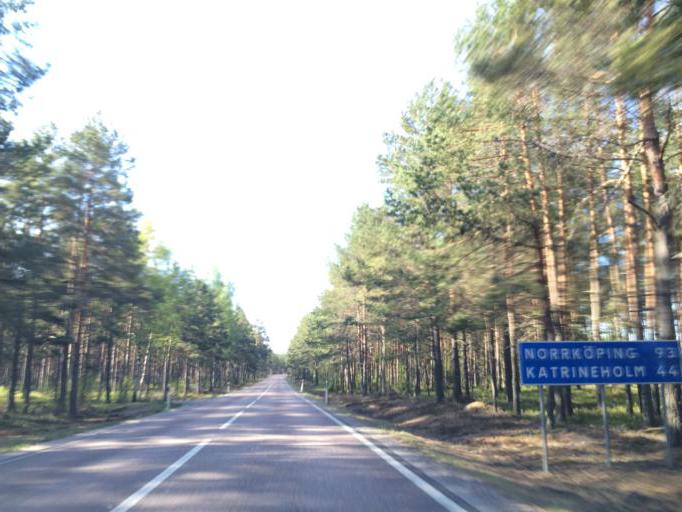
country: SE
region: Vaestmanland
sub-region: Kungsors Kommun
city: Kungsoer
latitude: 59.3463
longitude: 16.1119
